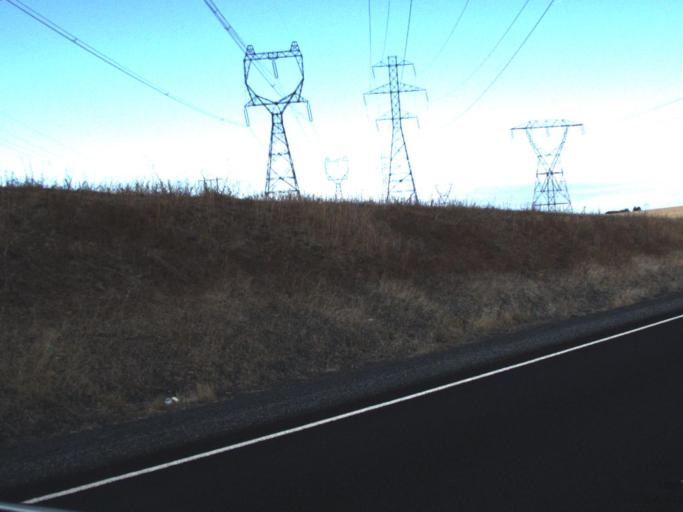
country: US
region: Washington
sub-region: Okanogan County
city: Coulee Dam
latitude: 47.8800
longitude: -118.8494
